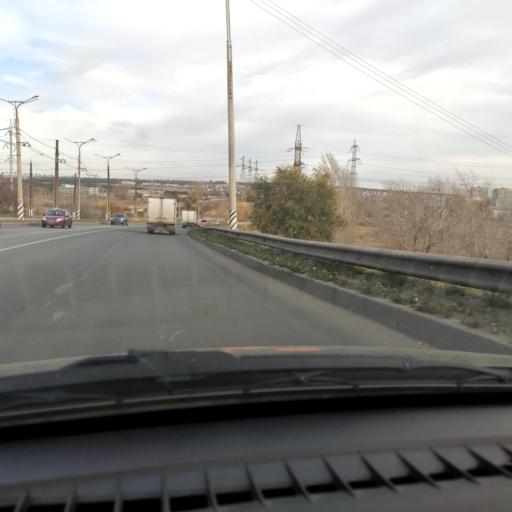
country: RU
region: Samara
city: Zhigulevsk
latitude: 53.4879
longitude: 49.5015
